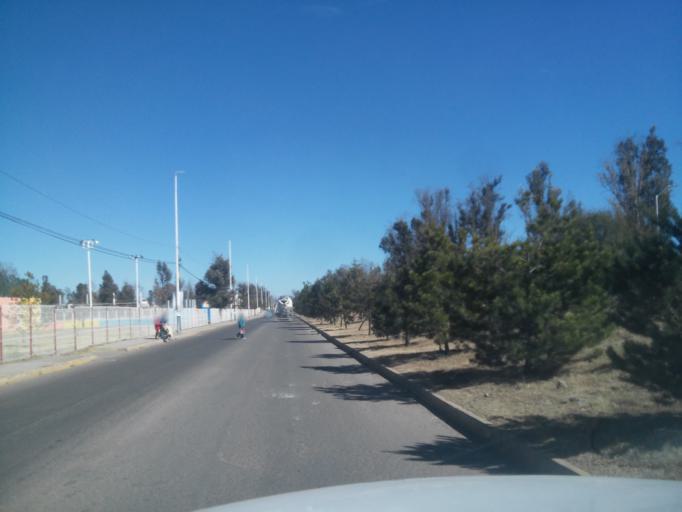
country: MX
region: Durango
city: Victoria de Durango
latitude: 24.0219
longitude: -104.6997
